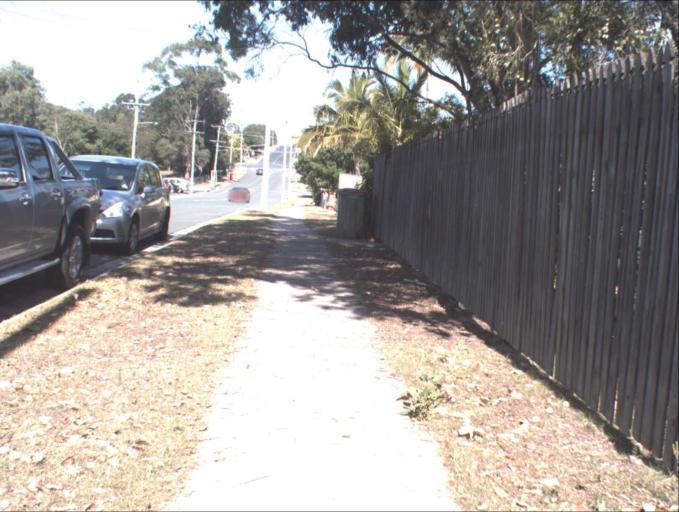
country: AU
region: Queensland
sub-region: Logan
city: Beenleigh
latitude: -27.6950
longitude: 153.2122
